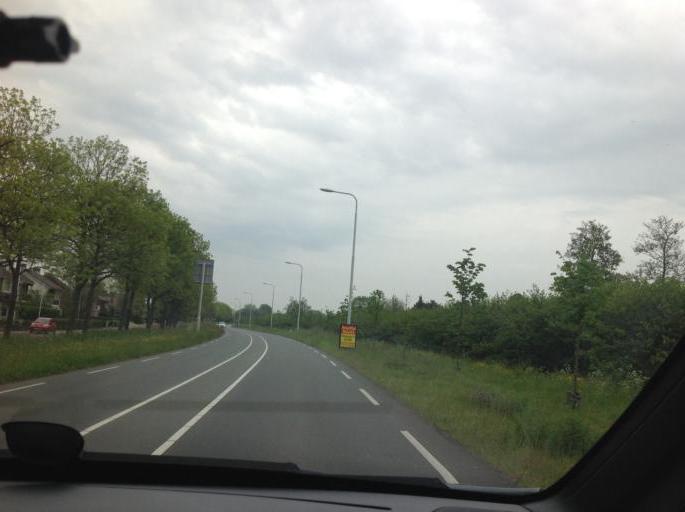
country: NL
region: Zeeland
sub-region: Gemeente Goes
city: Goes
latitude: 51.4963
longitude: 3.9131
